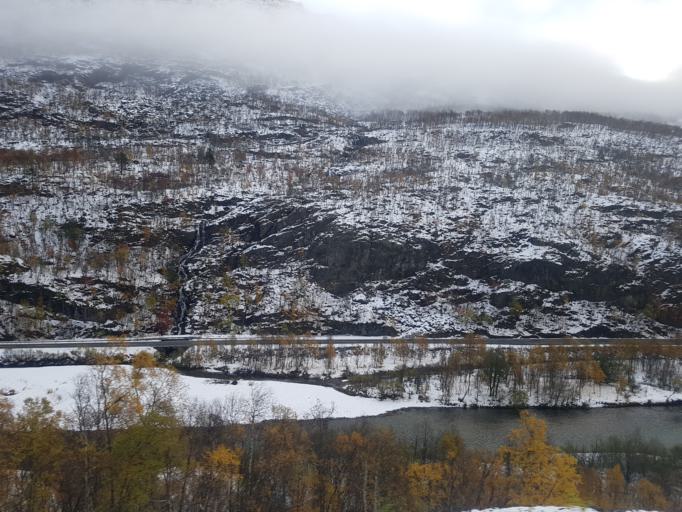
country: NO
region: Sor-Trondelag
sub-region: Oppdal
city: Oppdal
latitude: 62.3477
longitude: 9.6267
